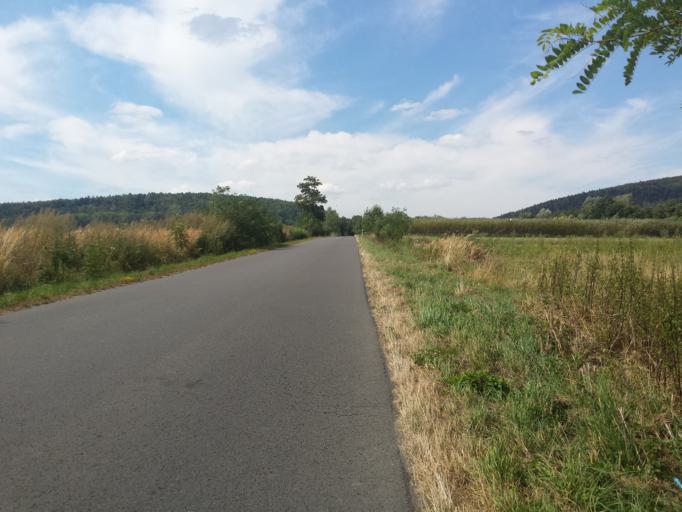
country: PL
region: Subcarpathian Voivodeship
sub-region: Powiat przemyski
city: Fredropol
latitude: 49.6722
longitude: 22.7419
